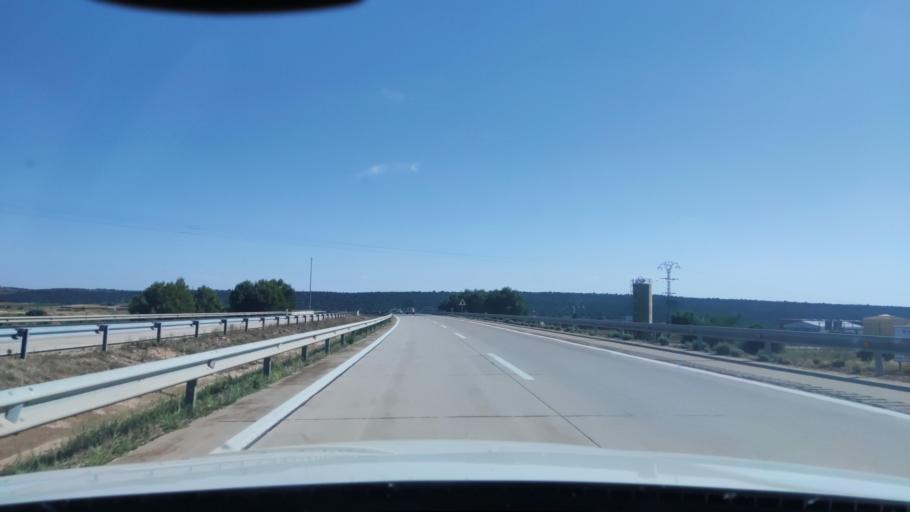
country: ES
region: Castille-La Mancha
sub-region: Provincia de Cuenca
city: Sisante
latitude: 39.4107
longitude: -2.2151
